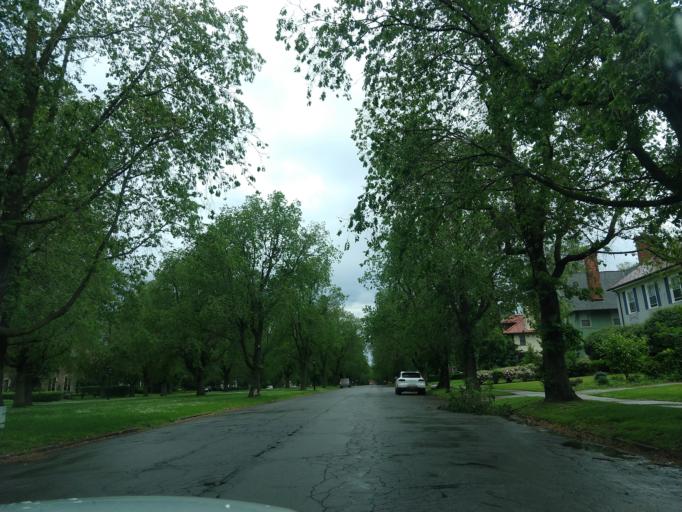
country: US
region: New York
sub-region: Erie County
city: Buffalo
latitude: 42.9226
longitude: -78.8699
